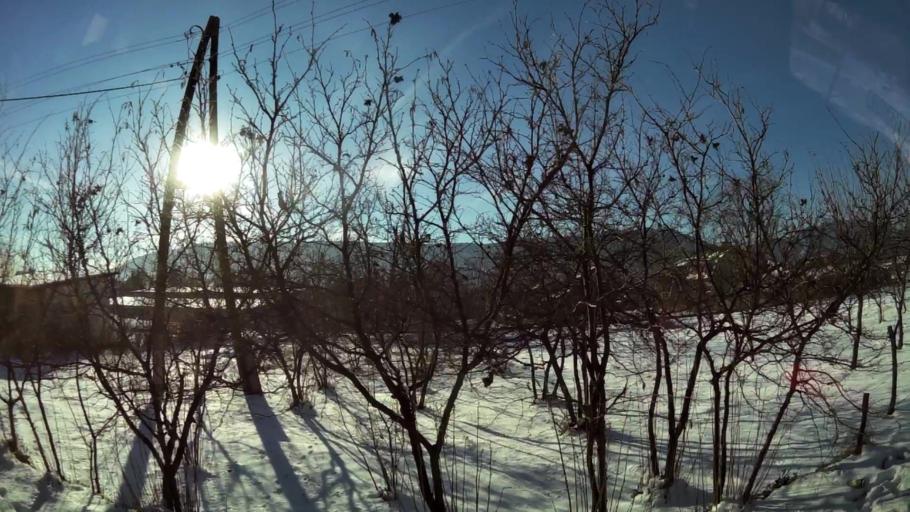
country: MK
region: Saraj
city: Saraj
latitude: 42.0112
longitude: 21.3426
